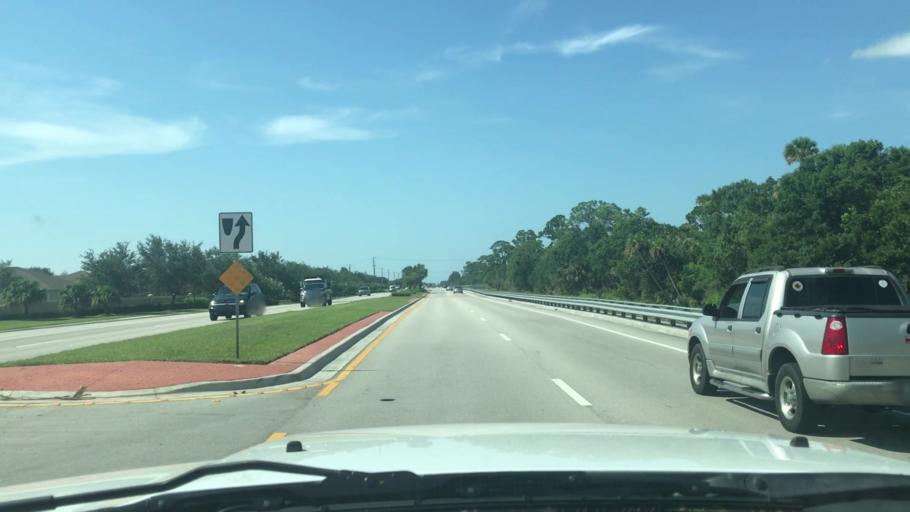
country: US
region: Florida
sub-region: Indian River County
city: West Vero Corridor
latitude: 27.6497
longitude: -80.4631
